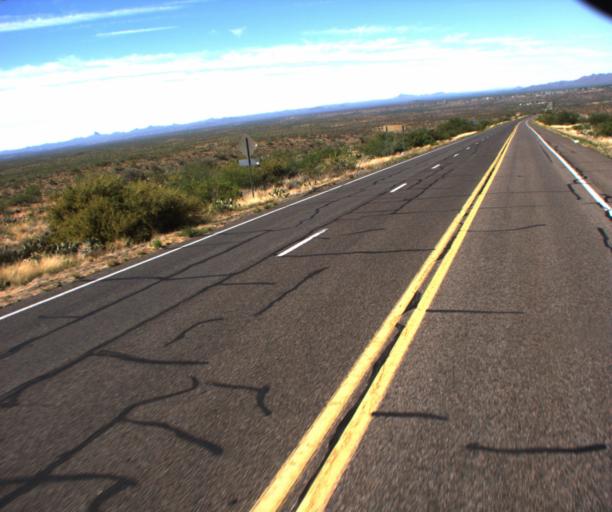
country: US
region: Arizona
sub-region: Yavapai County
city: Congress
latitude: 34.2042
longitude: -112.8043
